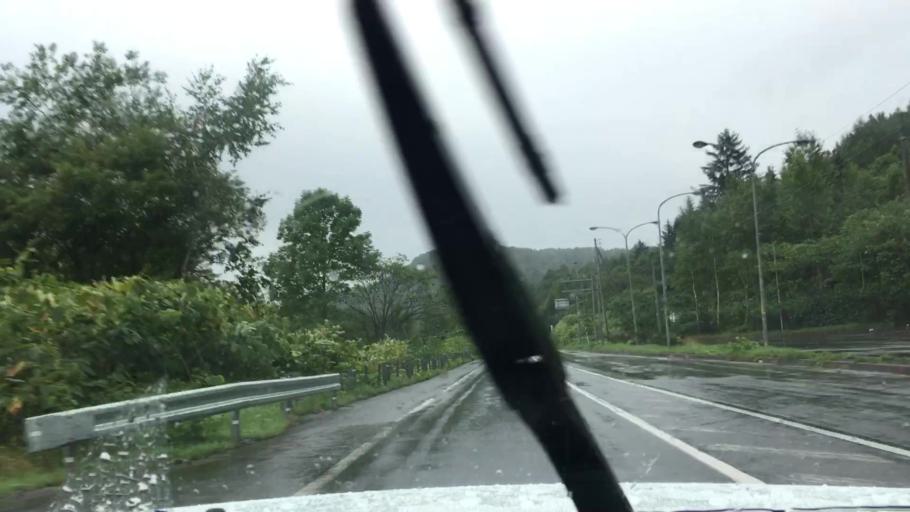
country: JP
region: Hokkaido
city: Niseko Town
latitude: 42.8303
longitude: 141.0087
